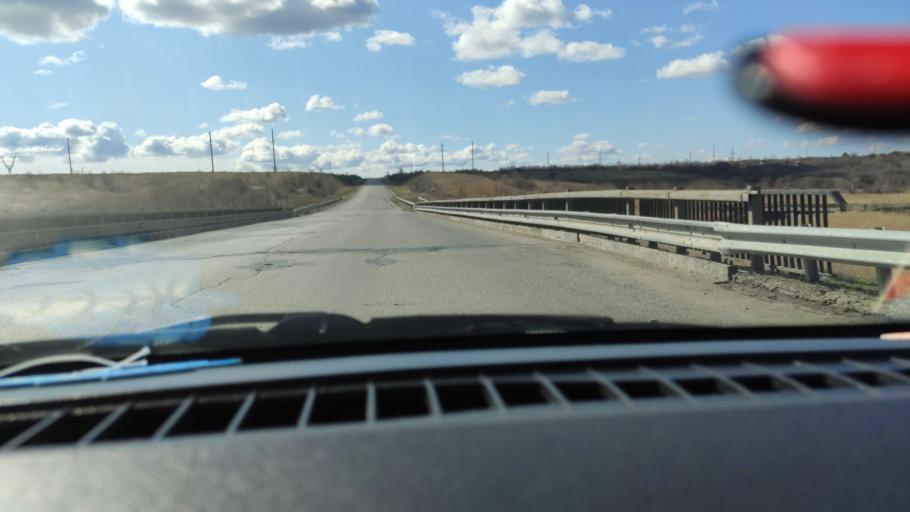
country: RU
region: Samara
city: Varlamovo
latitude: 53.0921
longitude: 48.3557
